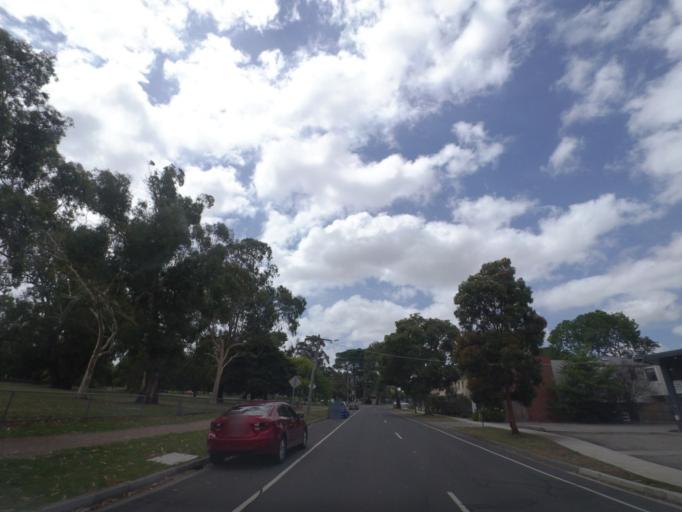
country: AU
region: Victoria
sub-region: Maroondah
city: Croydon South
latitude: -37.8002
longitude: 145.2851
